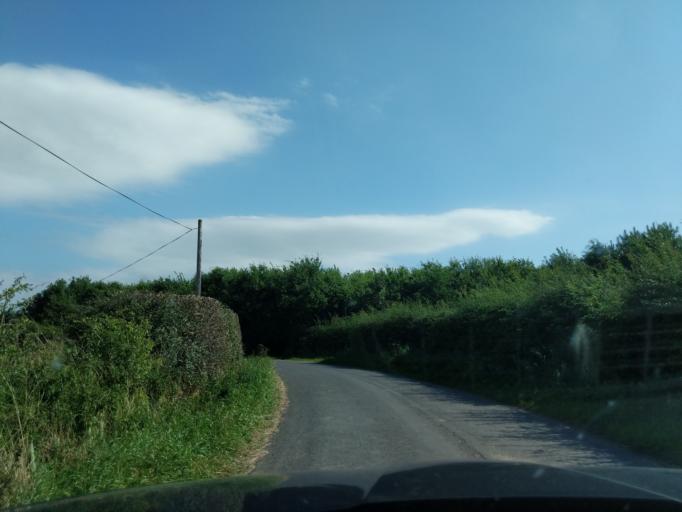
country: GB
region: Scotland
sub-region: The Scottish Borders
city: Coldstream
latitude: 55.6722
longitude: -2.1721
